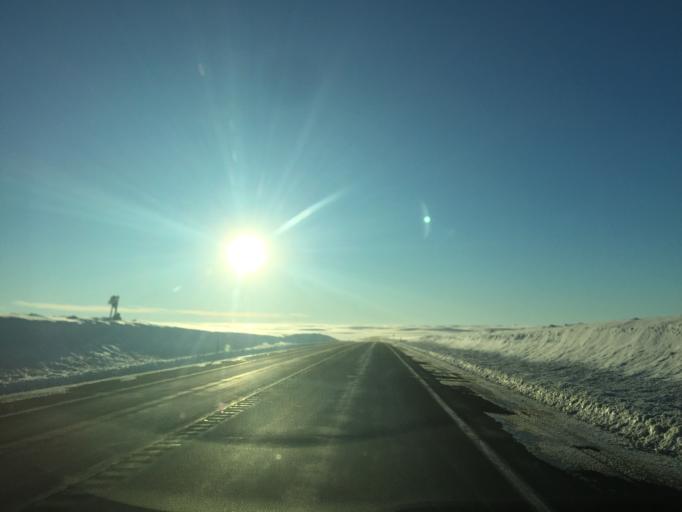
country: US
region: Washington
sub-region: Grant County
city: Soap Lake
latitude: 47.6111
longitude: -119.4837
